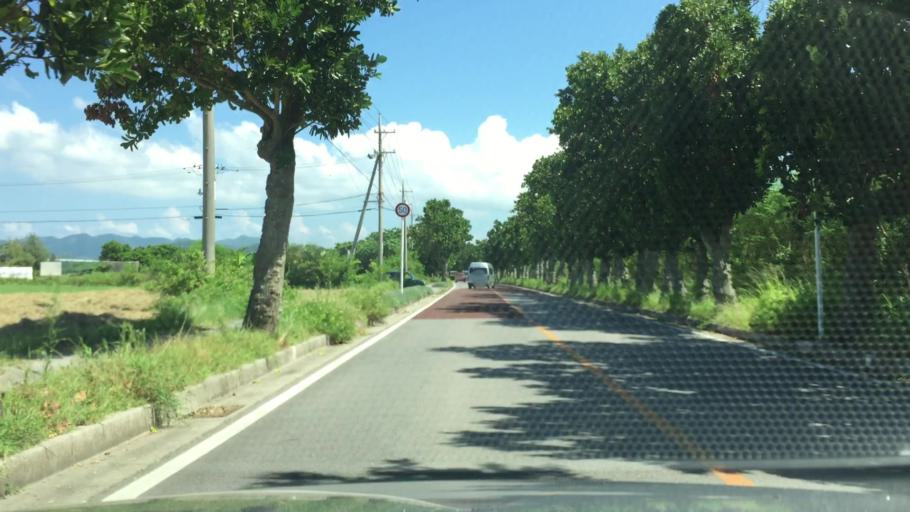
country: JP
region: Okinawa
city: Ishigaki
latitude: 24.3676
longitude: 124.2465
